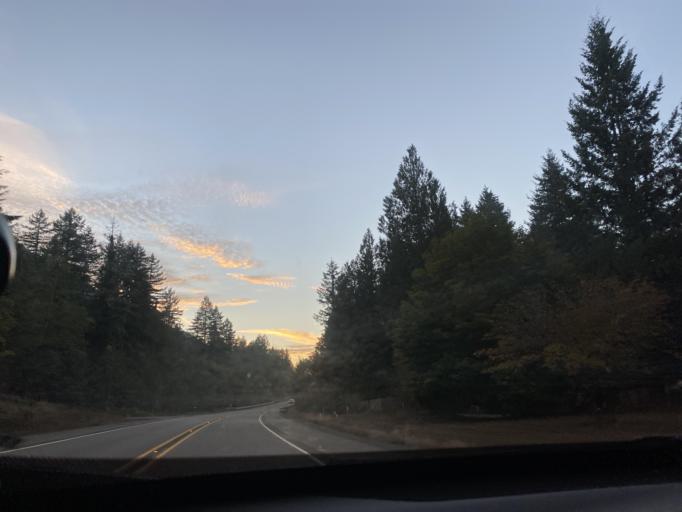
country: US
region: Washington
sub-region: Clallam County
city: Port Angeles
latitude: 48.0638
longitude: -123.5981
